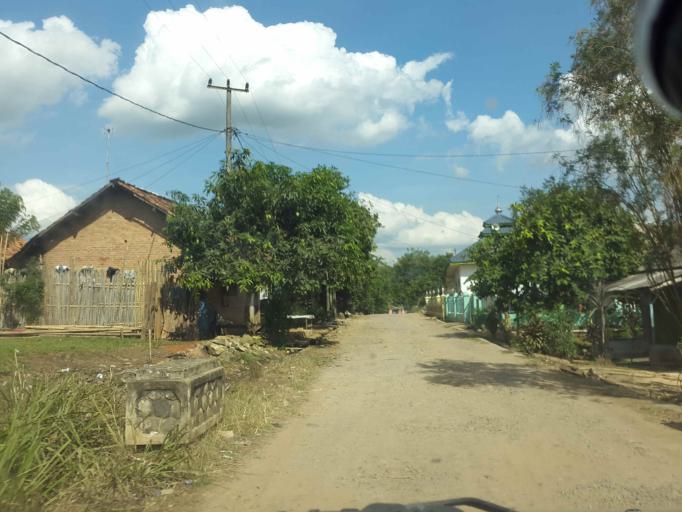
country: ID
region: Lampung
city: Panjang
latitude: -5.4209
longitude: 105.3511
